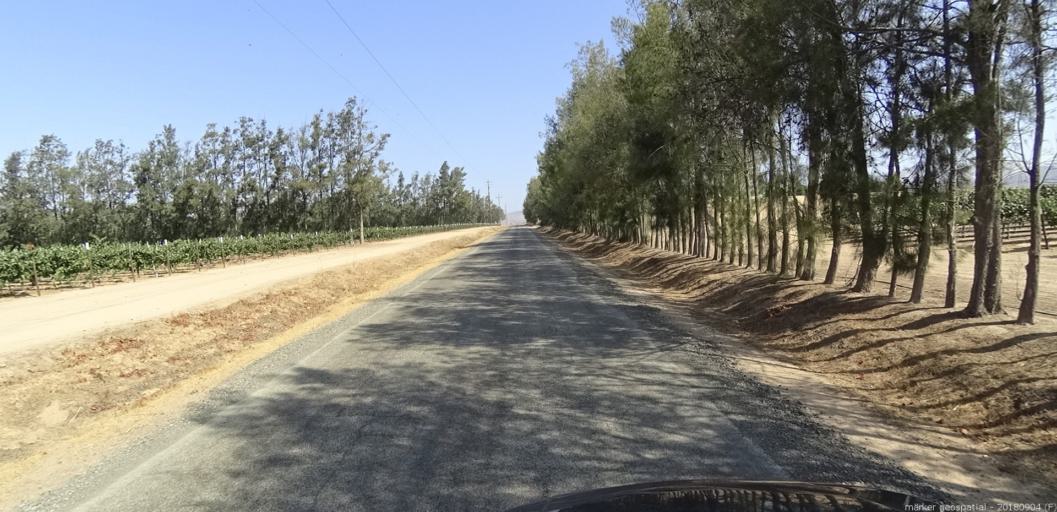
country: US
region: California
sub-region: Monterey County
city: Soledad
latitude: 36.4937
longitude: -121.3648
